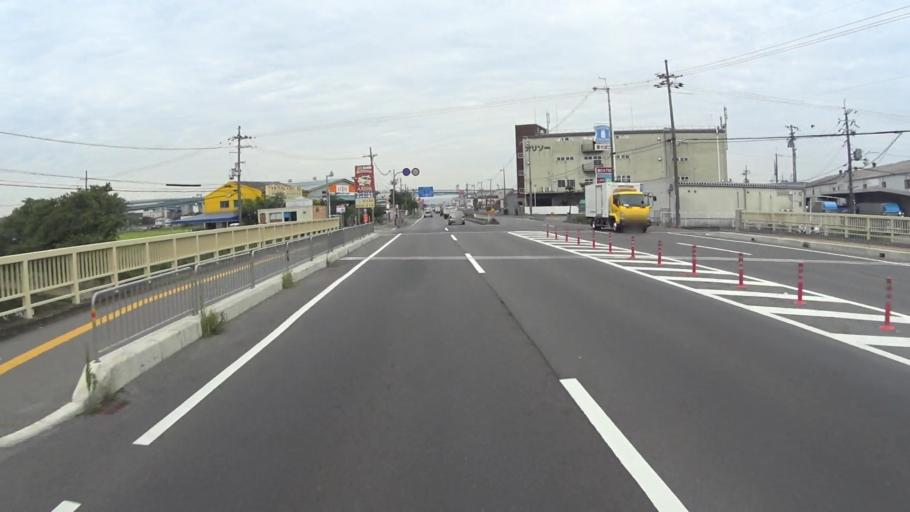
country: JP
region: Kyoto
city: Yawata
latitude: 34.9034
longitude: 135.7442
